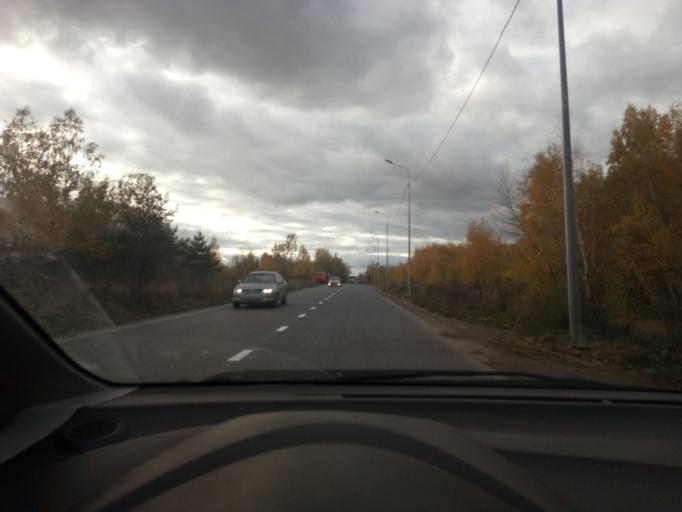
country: RU
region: Tatarstan
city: Staroye Arakchino
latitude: 55.8847
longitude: 48.9868
